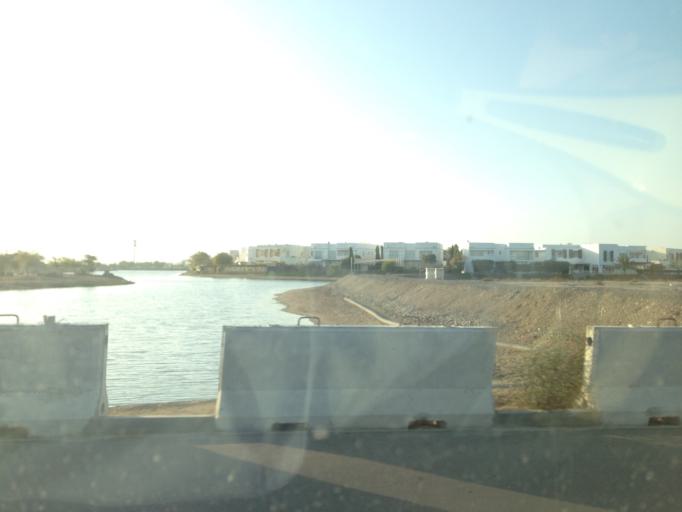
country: OM
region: Muhafazat Masqat
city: As Sib al Jadidah
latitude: 23.6211
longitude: 58.2731
